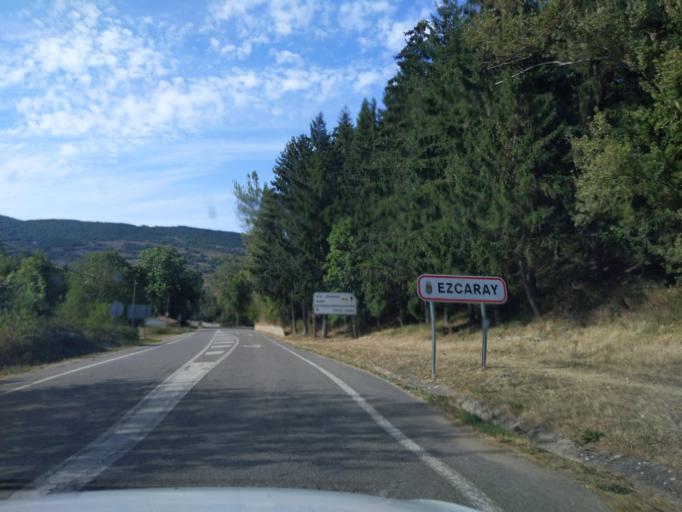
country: ES
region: La Rioja
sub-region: Provincia de La Rioja
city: Ezcaray
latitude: 42.3191
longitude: -3.0122
